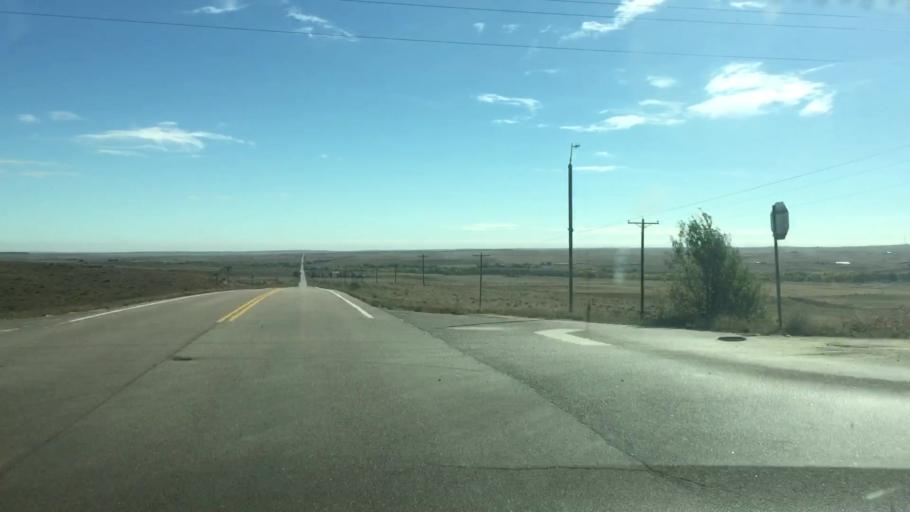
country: US
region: Colorado
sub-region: Elbert County
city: Kiowa
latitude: 39.2735
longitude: -104.1787
